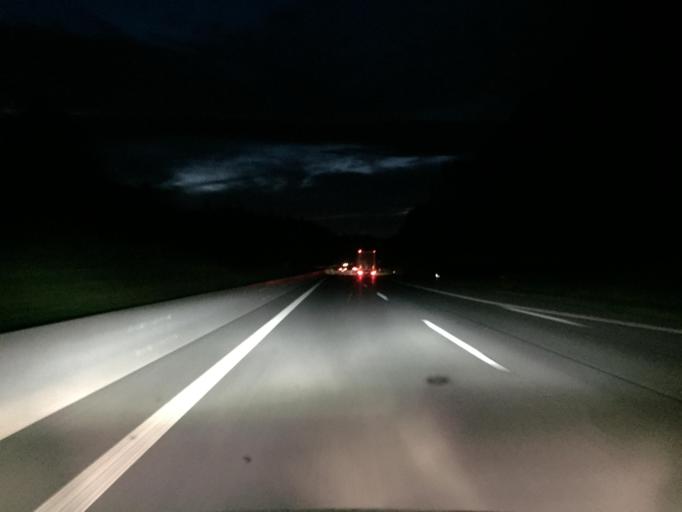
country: DE
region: Baden-Wuerttemberg
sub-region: Freiburg Region
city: Tuningen
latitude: 48.0727
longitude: 8.6038
